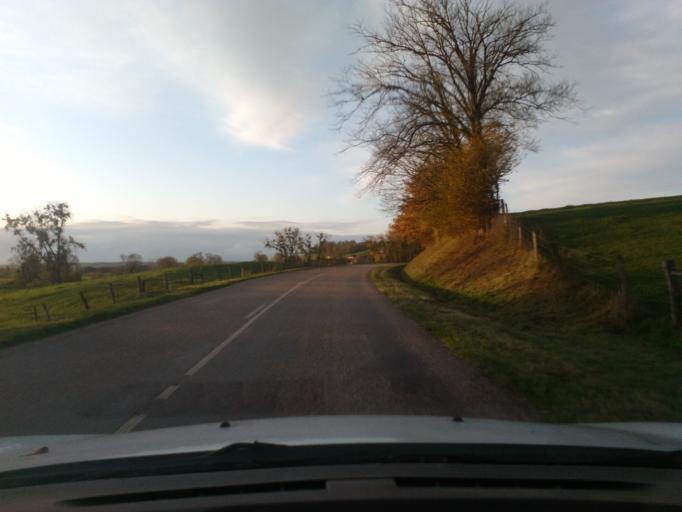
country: FR
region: Lorraine
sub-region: Departement des Vosges
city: Mirecourt
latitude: 48.2526
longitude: 6.1980
